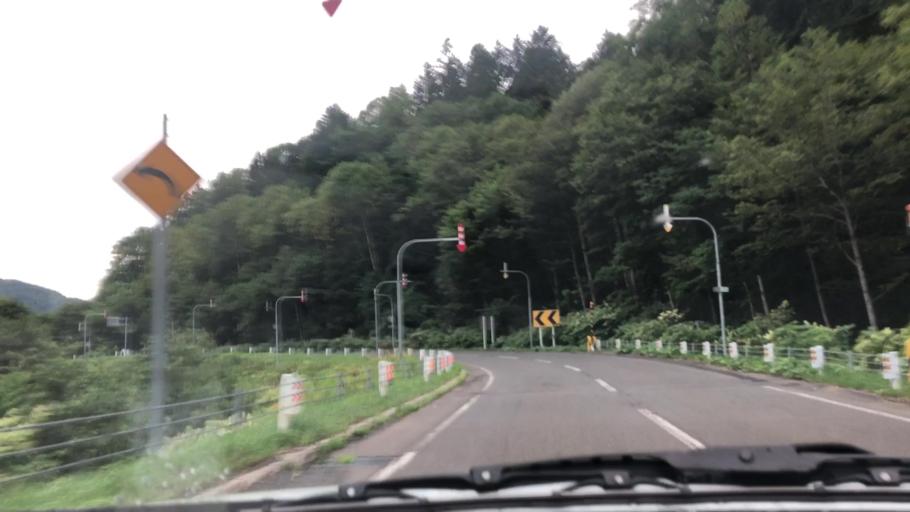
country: JP
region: Hokkaido
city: Shimo-furano
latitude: 42.9326
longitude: 142.3739
